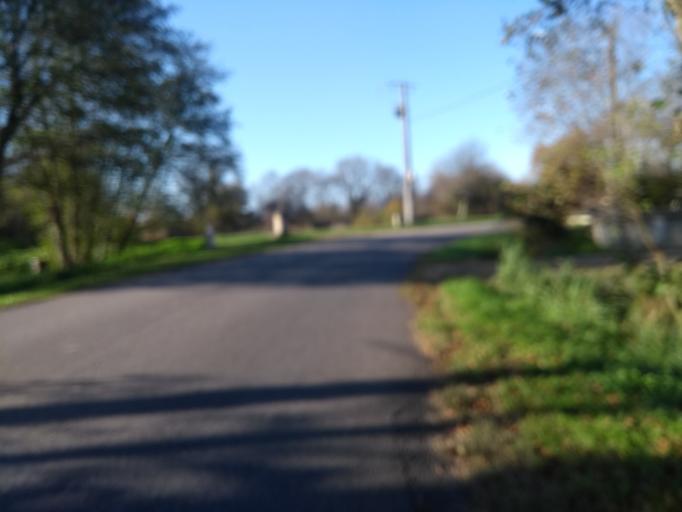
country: FR
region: Aquitaine
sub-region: Departement de la Gironde
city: Cambes
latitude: 44.7226
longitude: -0.4716
